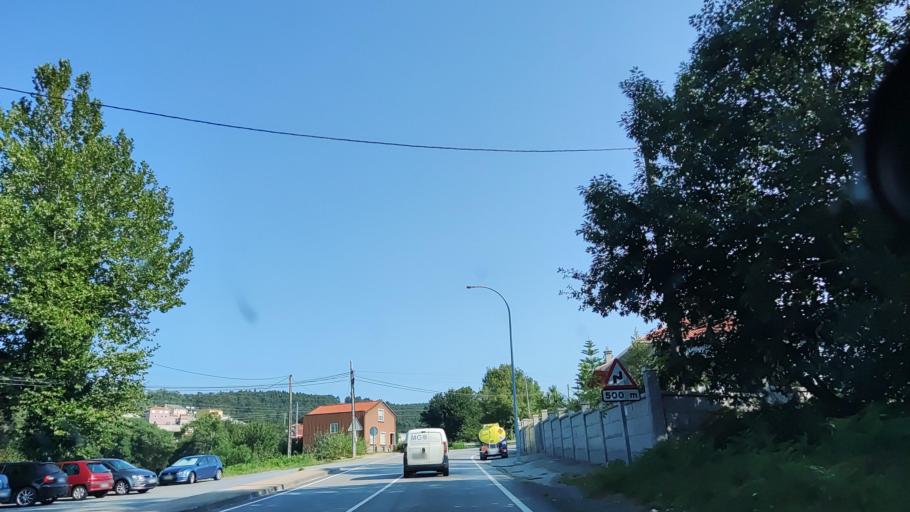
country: ES
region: Galicia
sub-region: Provincia da Coruna
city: Boiro
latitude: 42.6657
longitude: -8.8710
